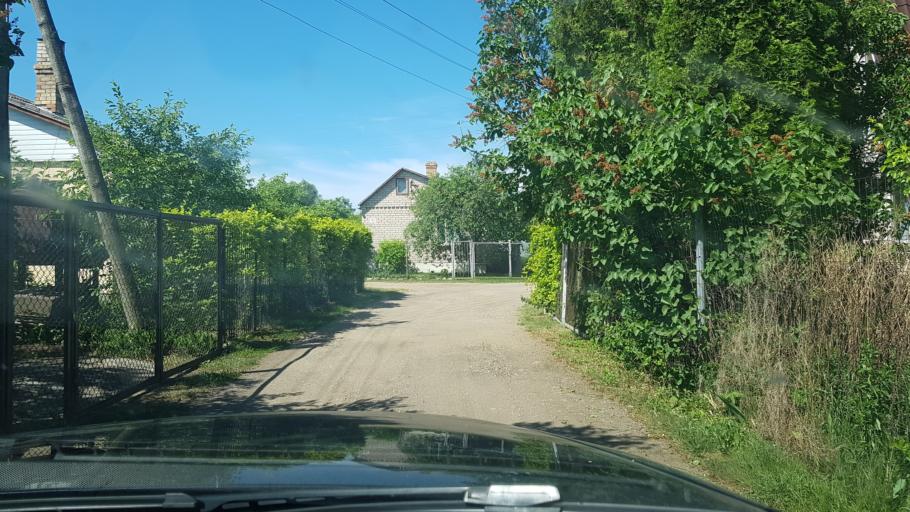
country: LV
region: Daugavpils
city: Daugavpils
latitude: 55.8602
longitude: 26.5744
